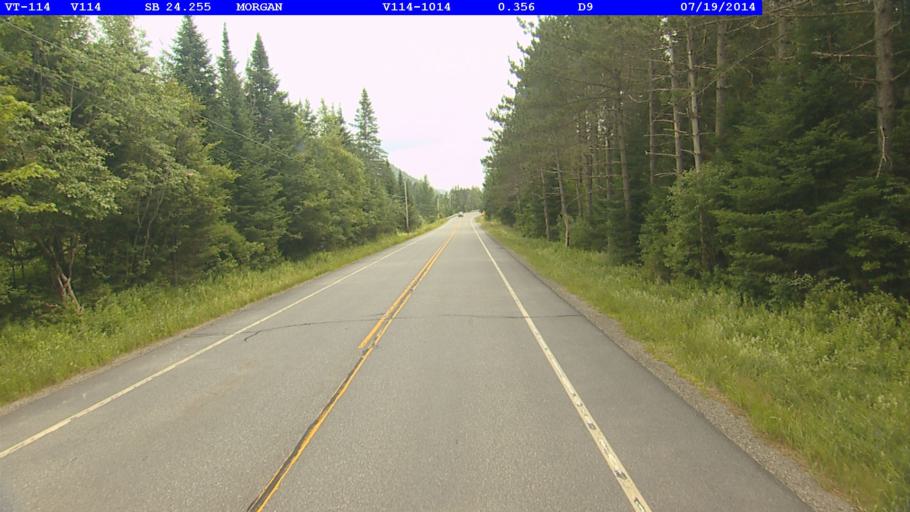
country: CA
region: Quebec
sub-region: Estrie
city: Coaticook
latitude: 44.8517
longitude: -71.9082
